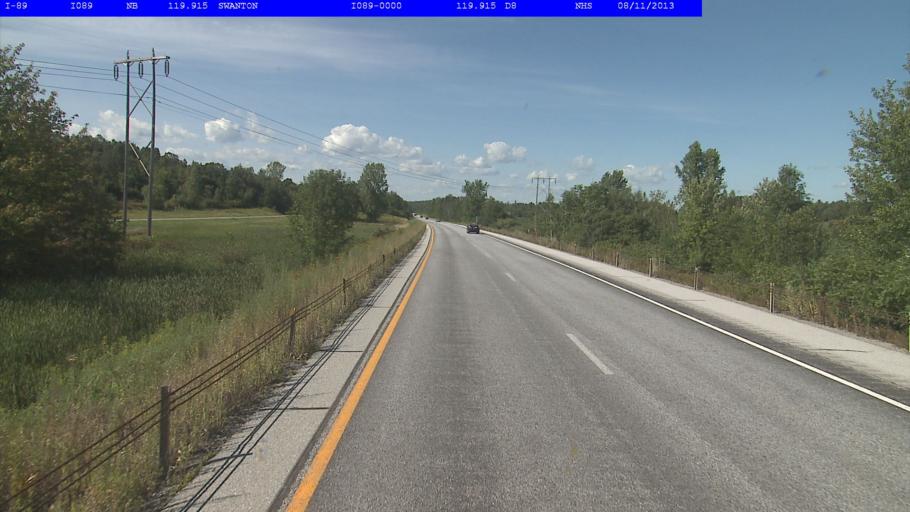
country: US
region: Vermont
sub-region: Franklin County
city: Swanton
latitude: 44.8758
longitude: -73.0827
